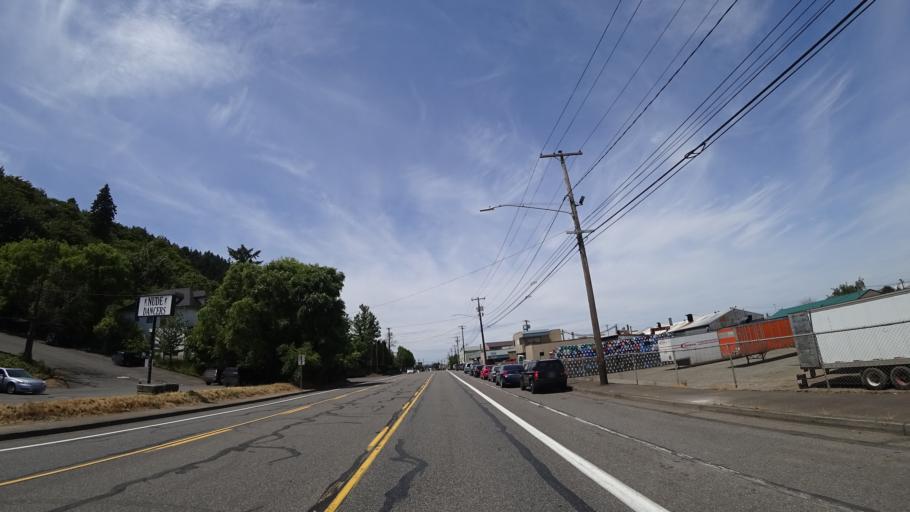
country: US
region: Oregon
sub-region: Multnomah County
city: Portland
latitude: 45.5430
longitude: -122.7208
